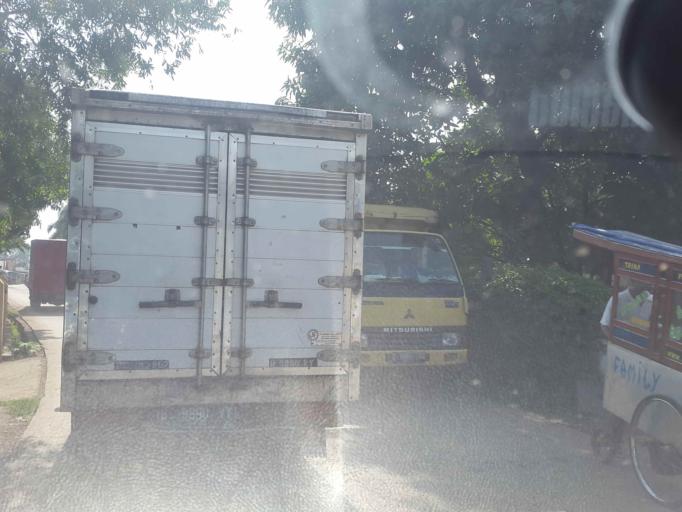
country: ID
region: West Java
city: Cikarang
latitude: -6.3637
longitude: 107.1125
